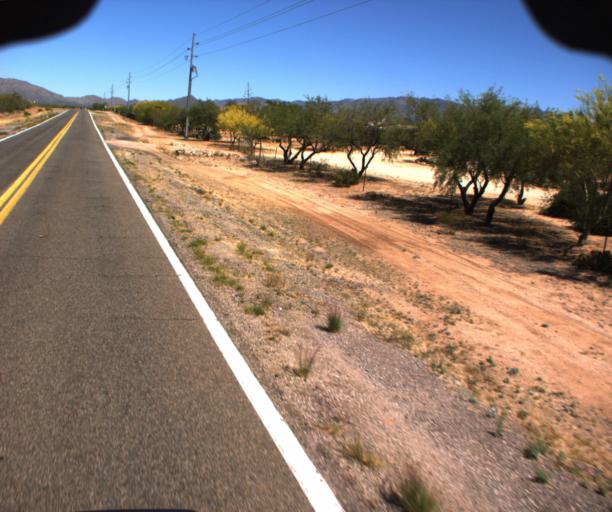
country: US
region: Arizona
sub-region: Yavapai County
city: Congress
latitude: 34.1197
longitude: -112.8358
